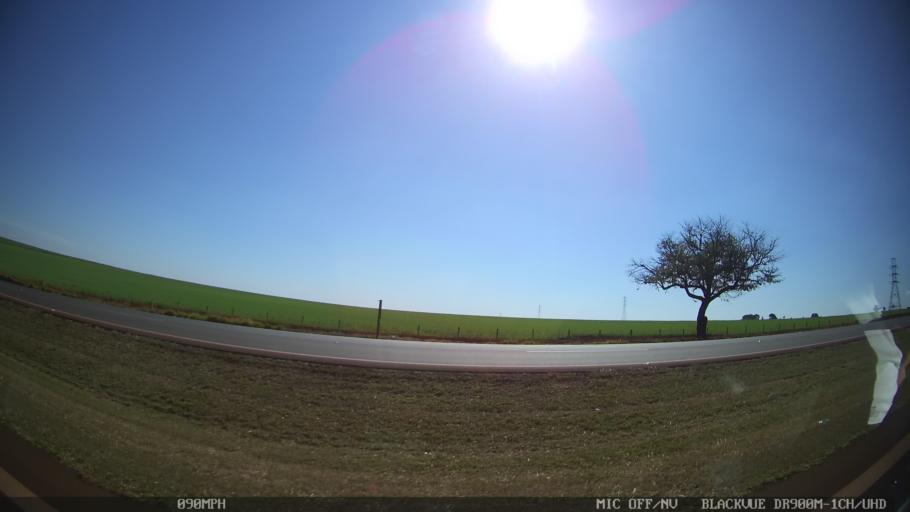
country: BR
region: Sao Paulo
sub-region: Ribeirao Preto
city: Ribeirao Preto
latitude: -21.1538
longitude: -47.8903
